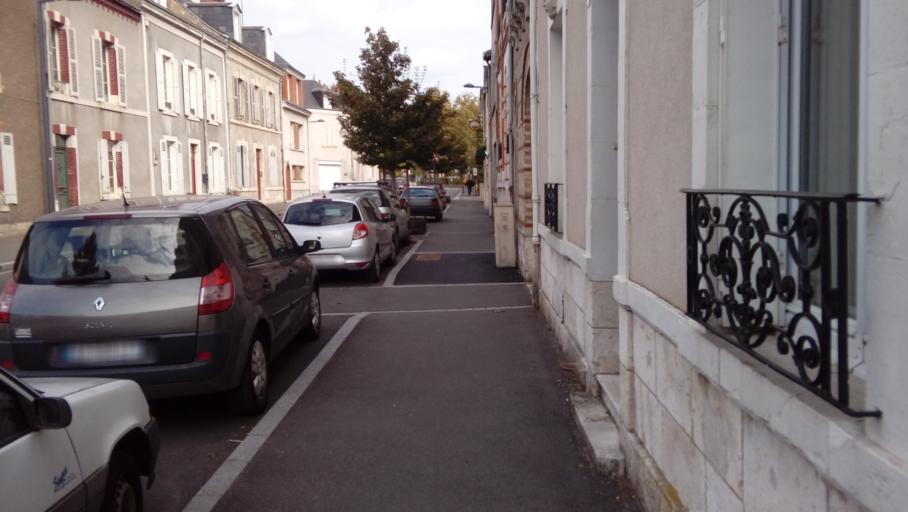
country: FR
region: Centre
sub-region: Departement du Loiret
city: Orleans
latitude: 47.9061
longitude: 1.8926
